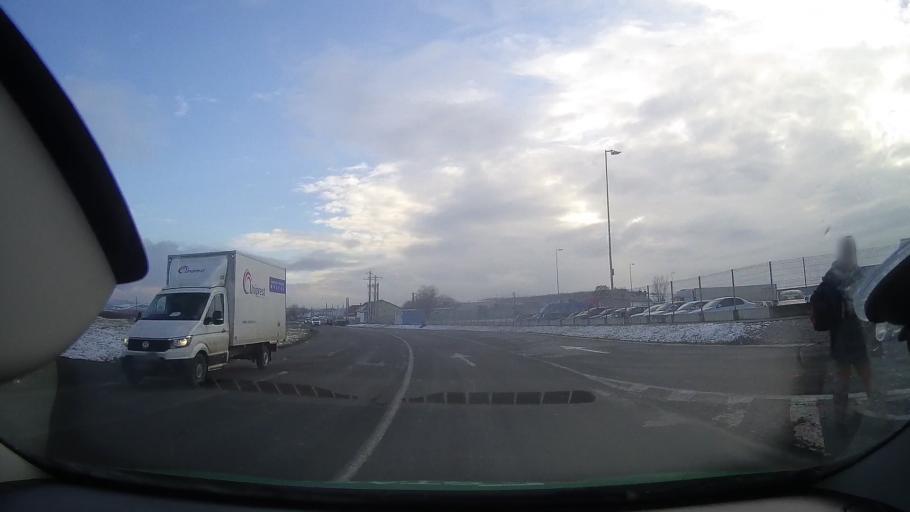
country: RO
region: Mures
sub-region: Comuna Iernut
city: Iernut
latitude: 46.4349
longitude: 24.2530
